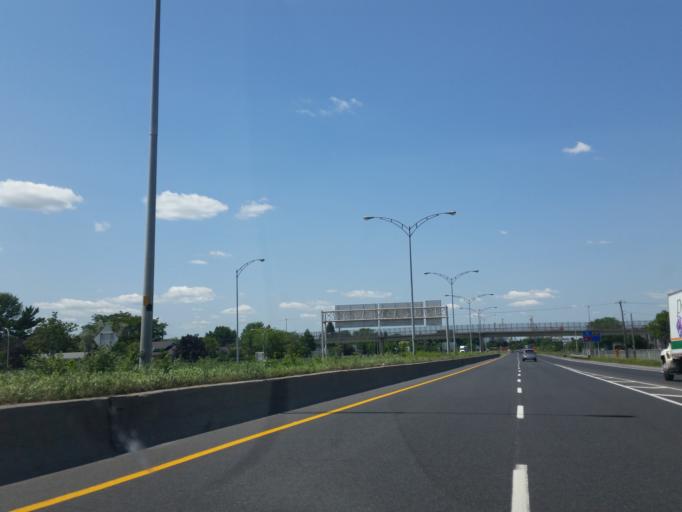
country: CA
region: Quebec
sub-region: Monteregie
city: Saint-Jean-sur-Richelieu
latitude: 45.3268
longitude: -73.2719
